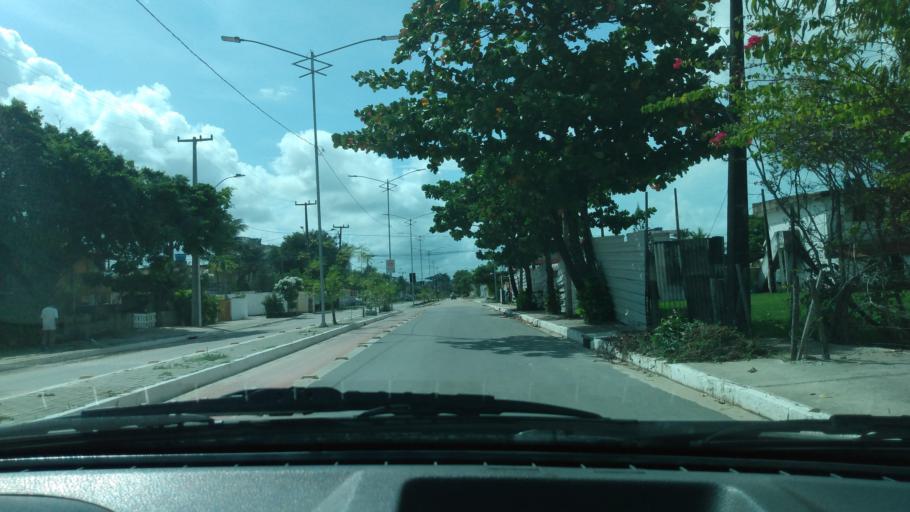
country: BR
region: Pernambuco
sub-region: Cabo De Santo Agostinho
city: Cabo
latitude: -8.3316
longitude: -34.9535
